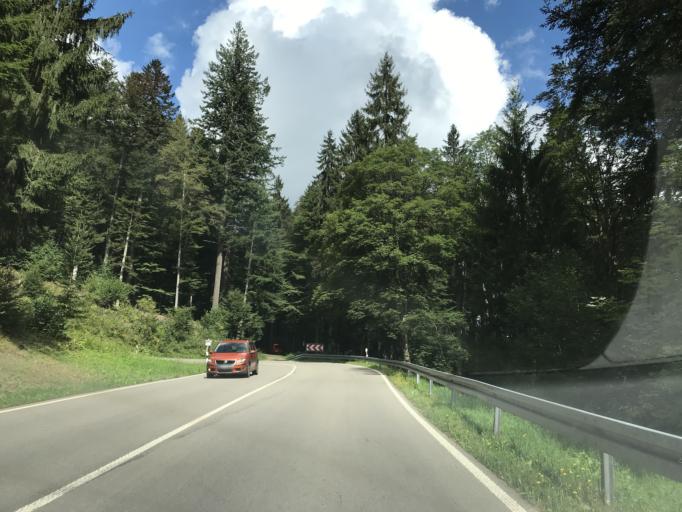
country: DE
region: Baden-Wuerttemberg
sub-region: Freiburg Region
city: Oberried
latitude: 47.8924
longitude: 7.9200
